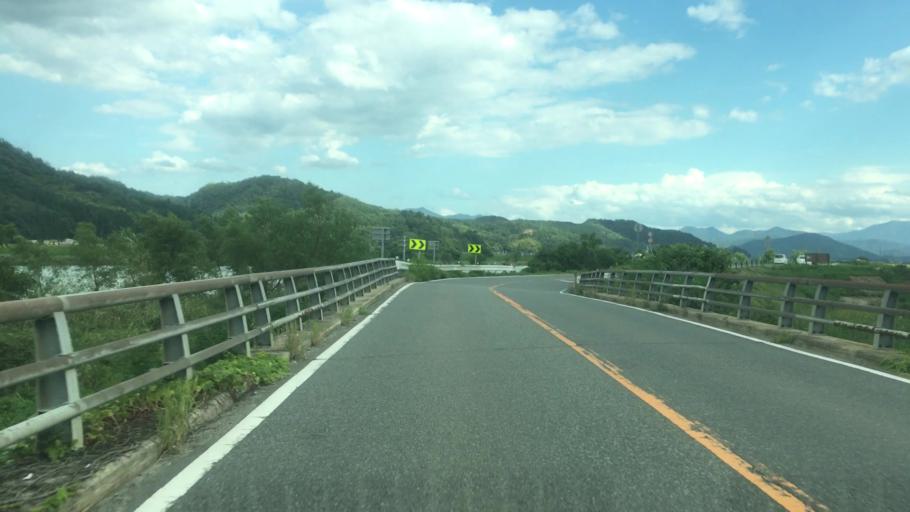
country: JP
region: Hyogo
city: Toyooka
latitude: 35.5744
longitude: 134.8057
